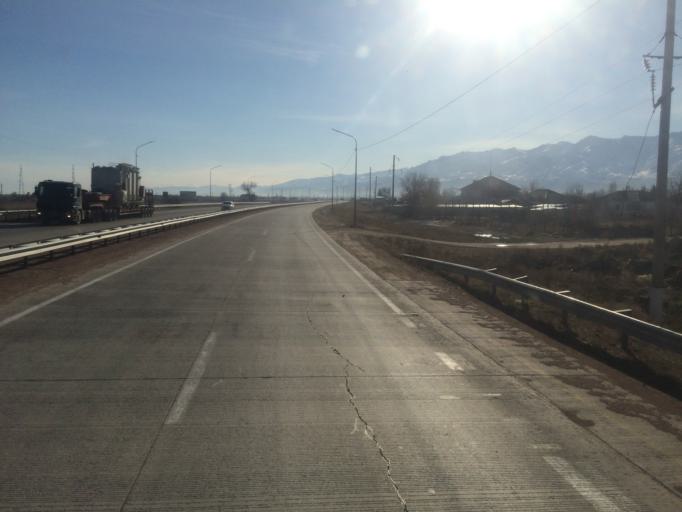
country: KG
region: Talas
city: Ivanovo-Alekseyevka
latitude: 42.9947
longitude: 72.1083
